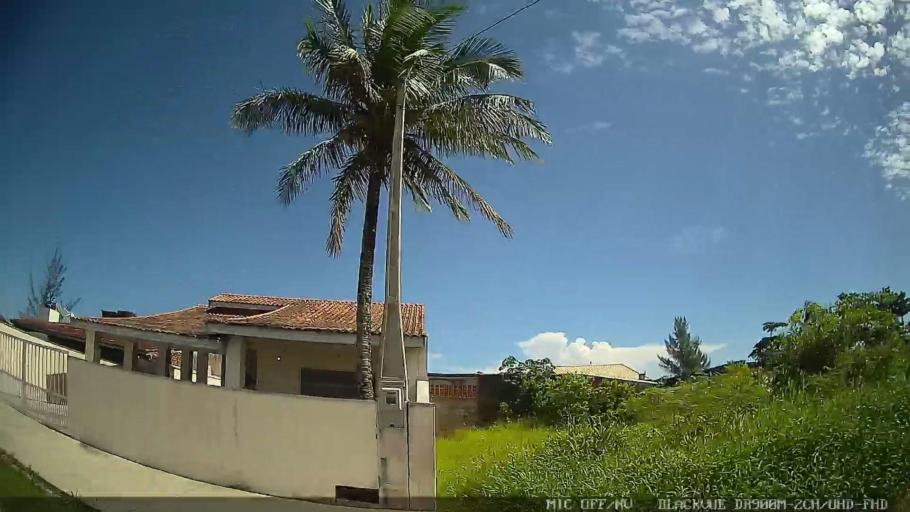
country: BR
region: Sao Paulo
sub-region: Iguape
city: Iguape
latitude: -24.7283
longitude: -47.5175
